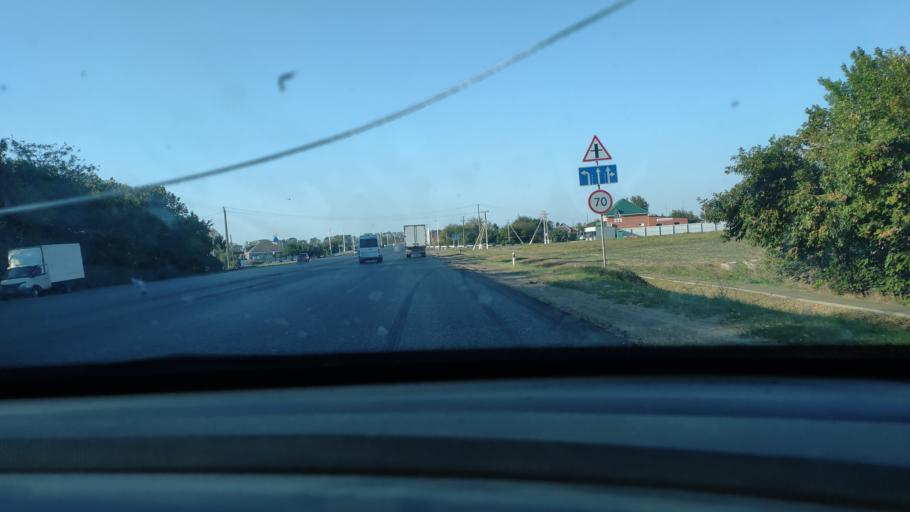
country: RU
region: Krasnodarskiy
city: Timashevsk
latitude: 45.5141
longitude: 38.9414
